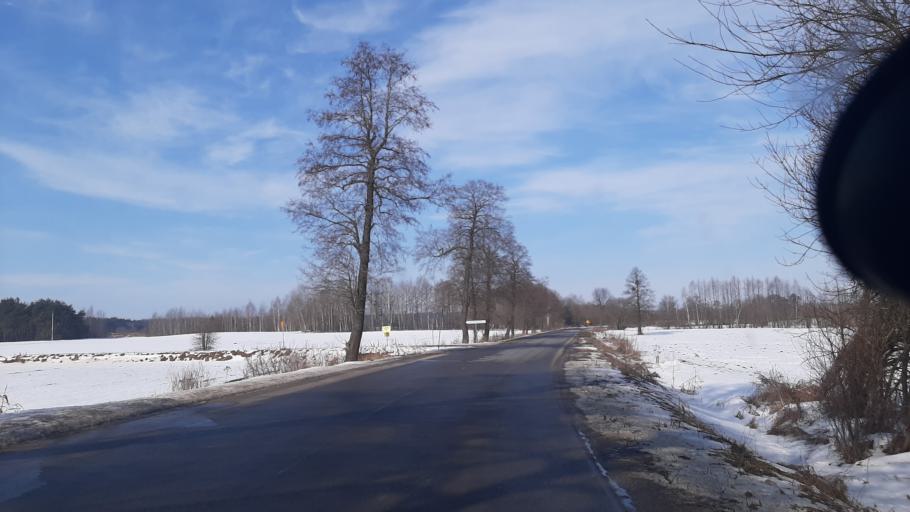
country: PL
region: Lublin Voivodeship
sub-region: Powiat pulawski
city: Kurow
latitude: 51.4129
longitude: 22.2030
